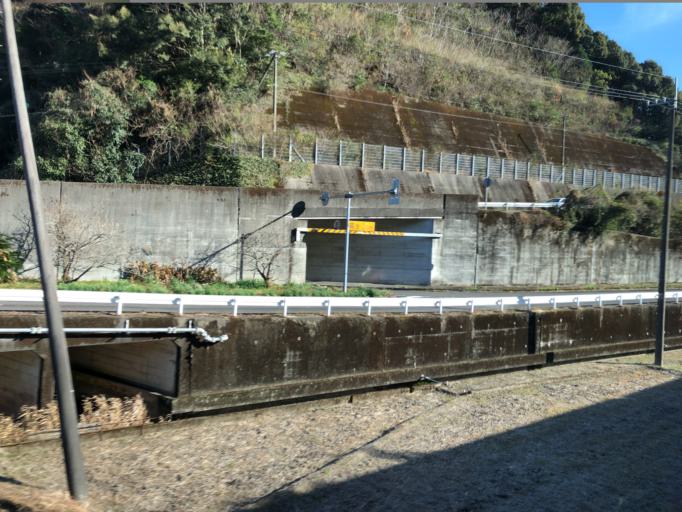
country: JP
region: Kochi
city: Nakamura
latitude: 33.1042
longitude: 133.0985
